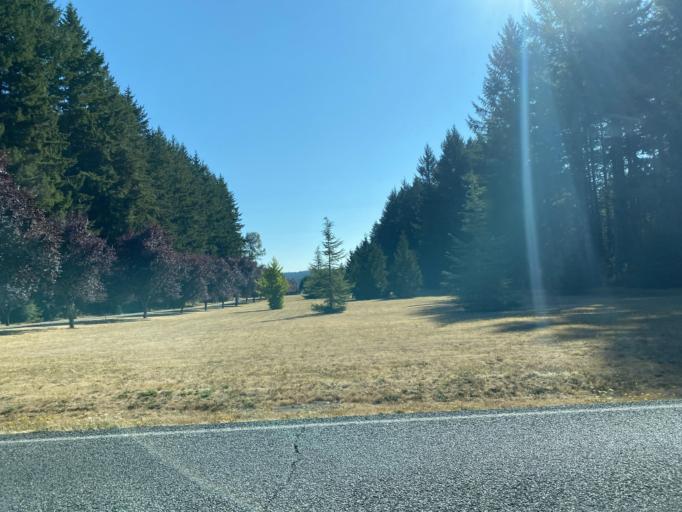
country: US
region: Washington
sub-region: Thurston County
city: Tanglewilde-Thompson Place
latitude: 46.9951
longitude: -122.7386
